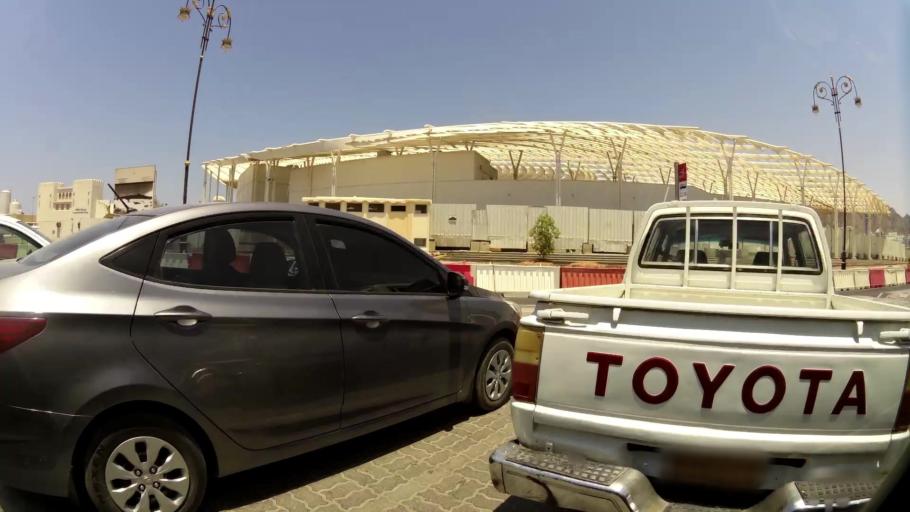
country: OM
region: Muhafazat Masqat
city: Muscat
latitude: 23.6247
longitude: 58.5624
